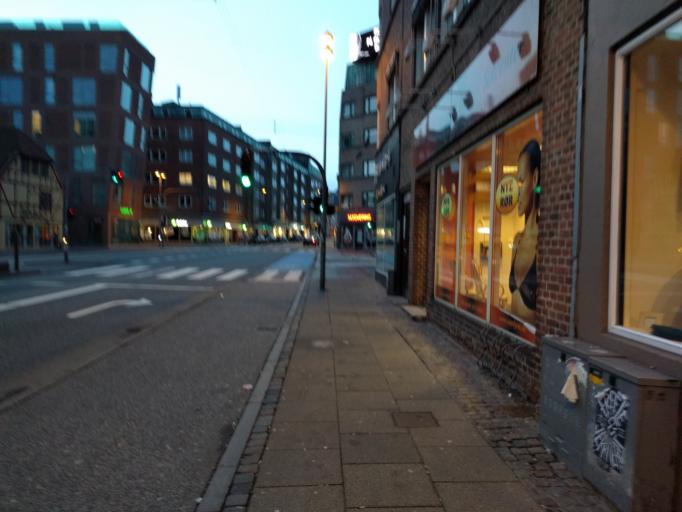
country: DK
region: North Denmark
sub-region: Alborg Kommune
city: Aalborg
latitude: 57.0497
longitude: 9.9163
